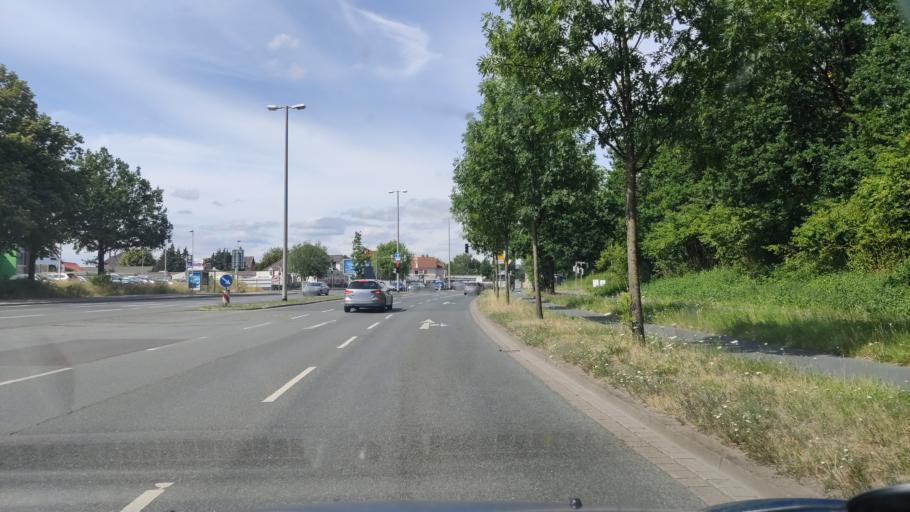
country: DE
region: Lower Saxony
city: Ronnenberg
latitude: 52.3485
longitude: 9.6896
